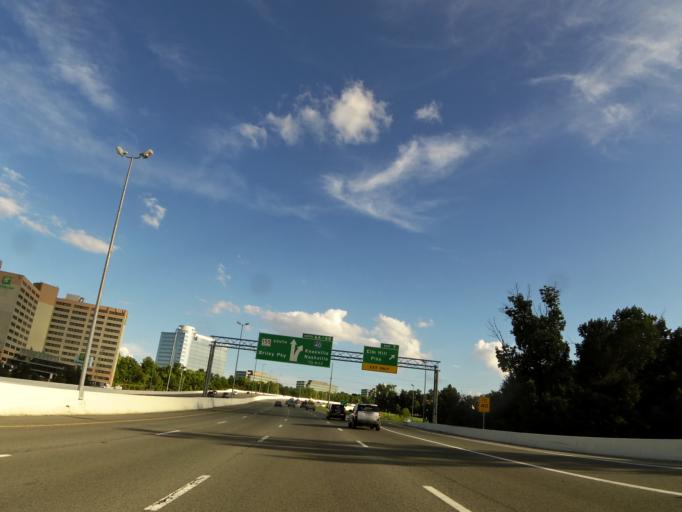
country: US
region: Tennessee
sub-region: Davidson County
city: Nashville
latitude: 36.1552
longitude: -86.6923
